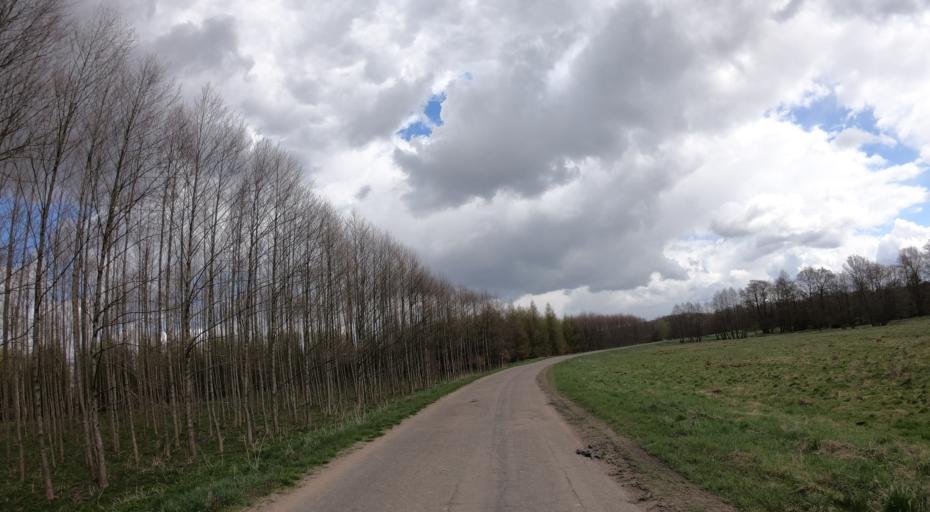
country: PL
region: West Pomeranian Voivodeship
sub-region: Powiat drawski
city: Drawsko Pomorskie
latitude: 53.5410
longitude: 15.8783
